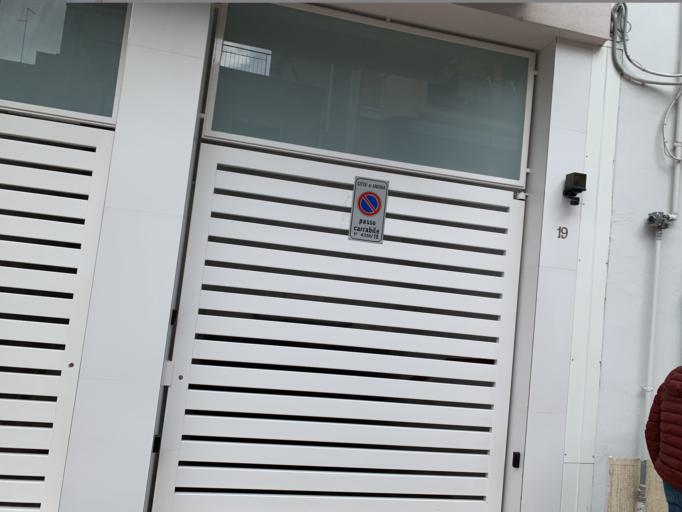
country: IT
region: Apulia
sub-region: Provincia di Barletta - Andria - Trani
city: Andria
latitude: 41.2349
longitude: 16.2941
